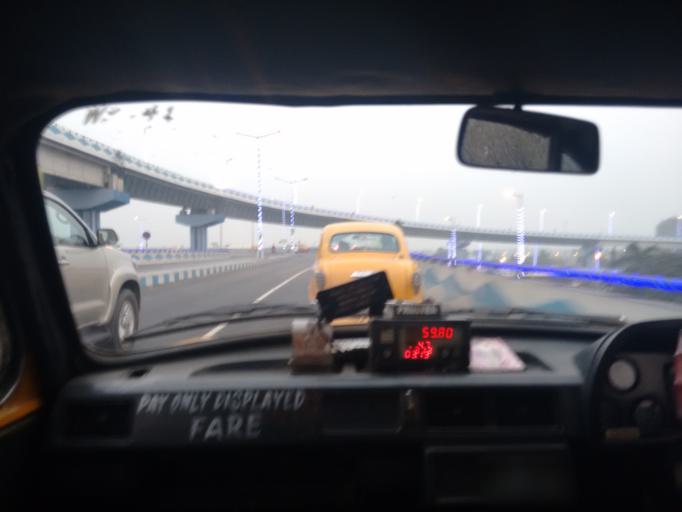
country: IN
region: West Bengal
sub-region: Kolkata
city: Kolkata
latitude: 22.5431
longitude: 88.3968
